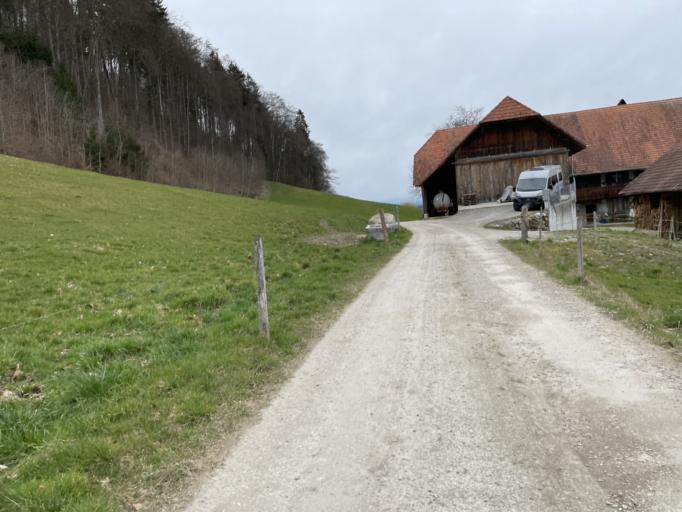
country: CH
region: Bern
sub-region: Bern-Mittelland District
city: Rubigen
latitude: 46.8843
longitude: 7.5269
